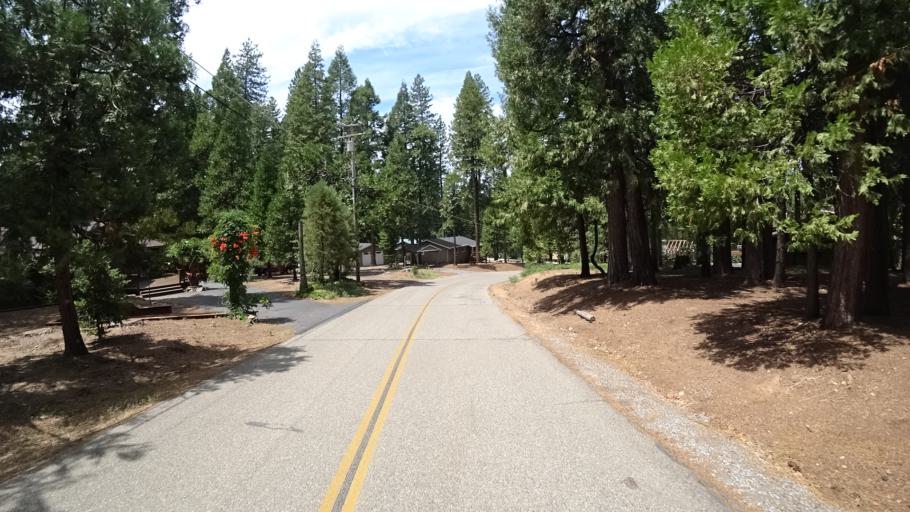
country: US
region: California
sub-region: Calaveras County
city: Arnold
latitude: 38.2374
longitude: -120.3596
